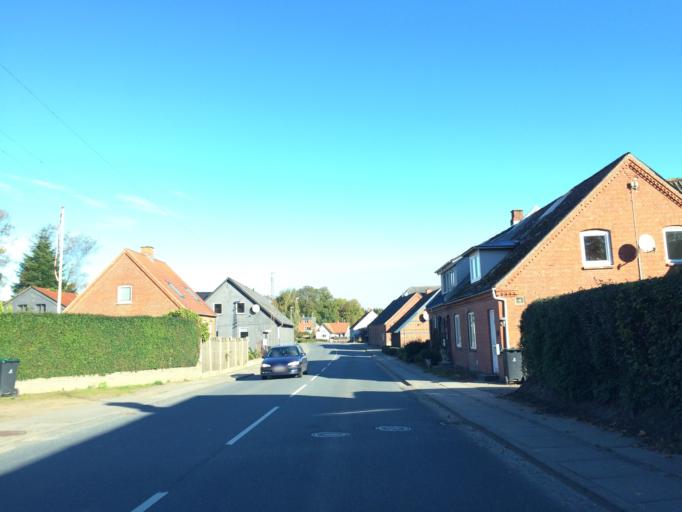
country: DK
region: Central Jutland
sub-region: Randers Kommune
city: Langa
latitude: 56.3444
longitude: 9.8737
